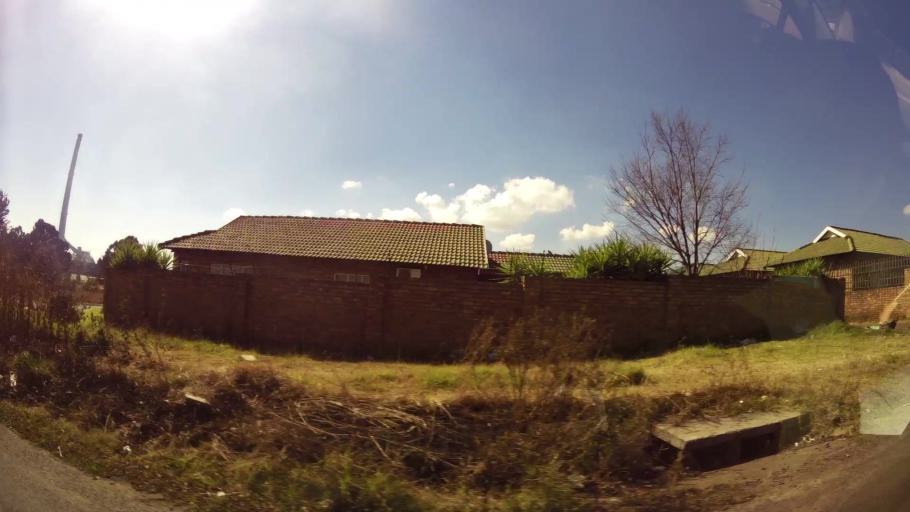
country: ZA
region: Mpumalanga
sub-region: Nkangala District Municipality
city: Witbank
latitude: -25.8671
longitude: 29.2259
